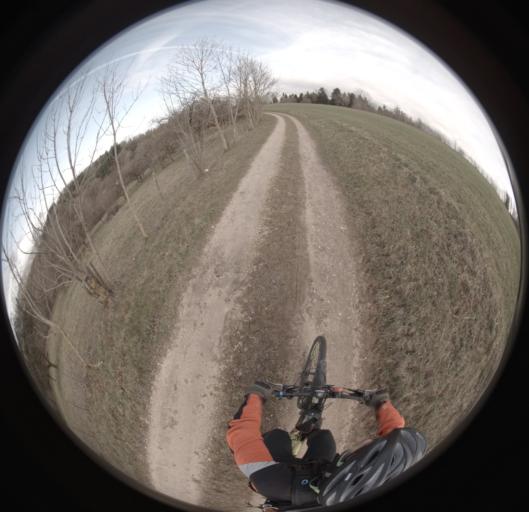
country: DE
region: Baden-Wuerttemberg
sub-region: Regierungsbezirk Stuttgart
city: Waschenbeuren
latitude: 48.7415
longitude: 9.6937
